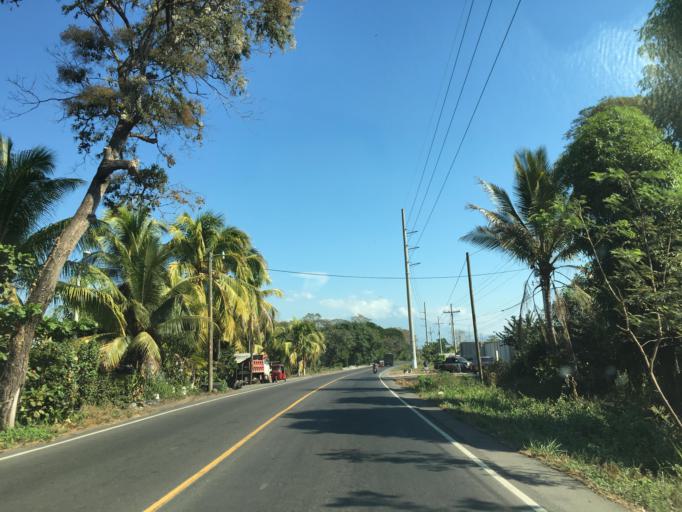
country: GT
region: Escuintla
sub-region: Municipio de La Democracia
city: La Democracia
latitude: 14.2100
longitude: -90.9569
